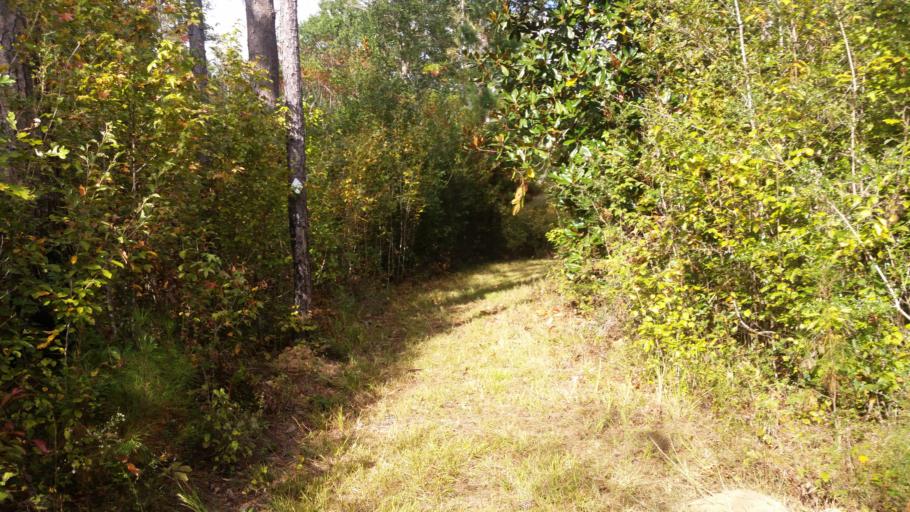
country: US
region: Mississippi
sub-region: Stone County
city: Wiggins
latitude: 30.9915
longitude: -89.0538
